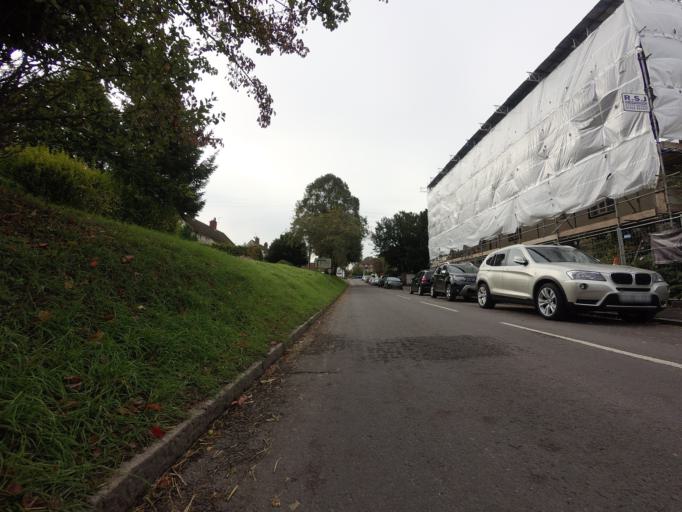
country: GB
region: England
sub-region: Cambridgeshire
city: Melbourn
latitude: 52.0274
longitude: 0.0384
